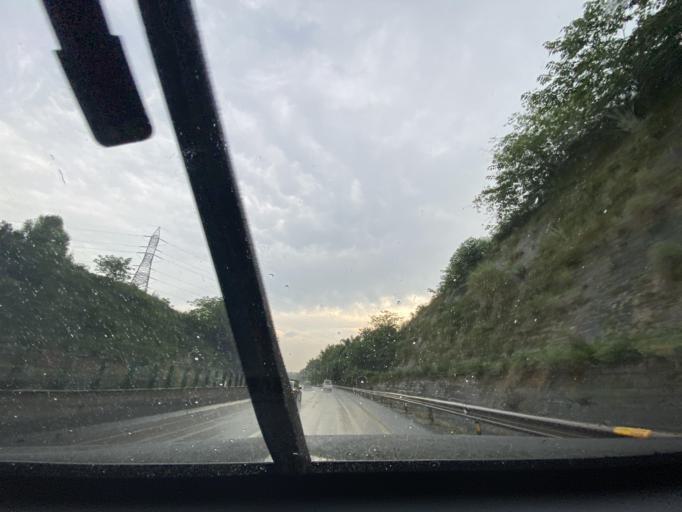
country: CN
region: Sichuan
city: Chonglong
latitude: 29.7630
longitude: 104.8182
